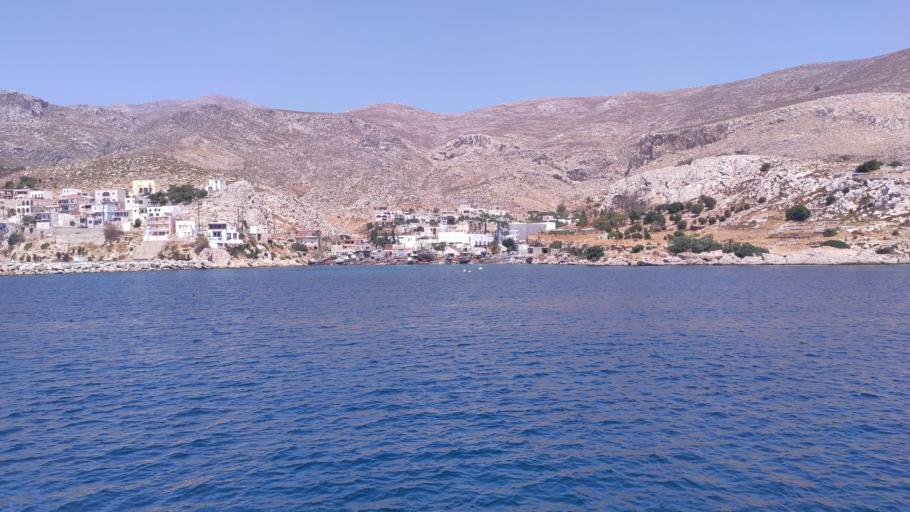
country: GR
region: South Aegean
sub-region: Nomos Dodekanisou
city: Kalymnos
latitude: 36.9483
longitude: 26.9950
